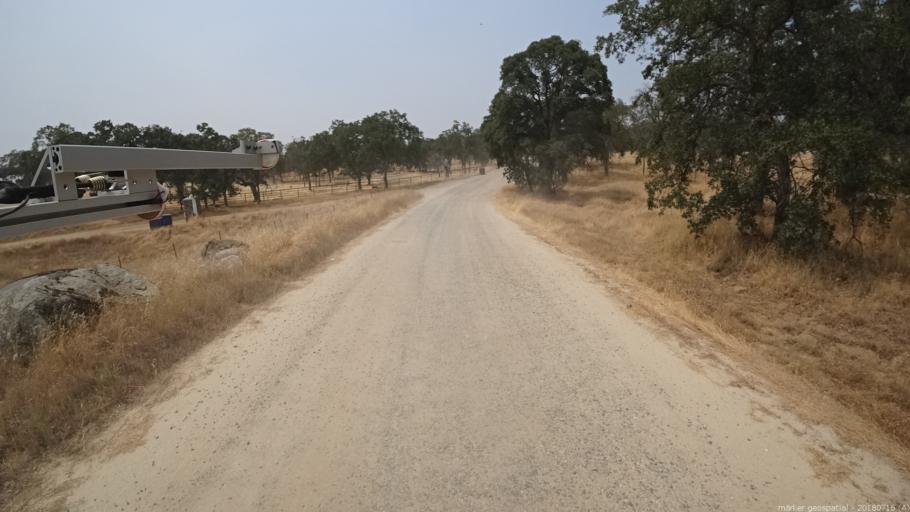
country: US
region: California
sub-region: Madera County
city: Yosemite Lakes
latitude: 37.2311
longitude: -119.7917
